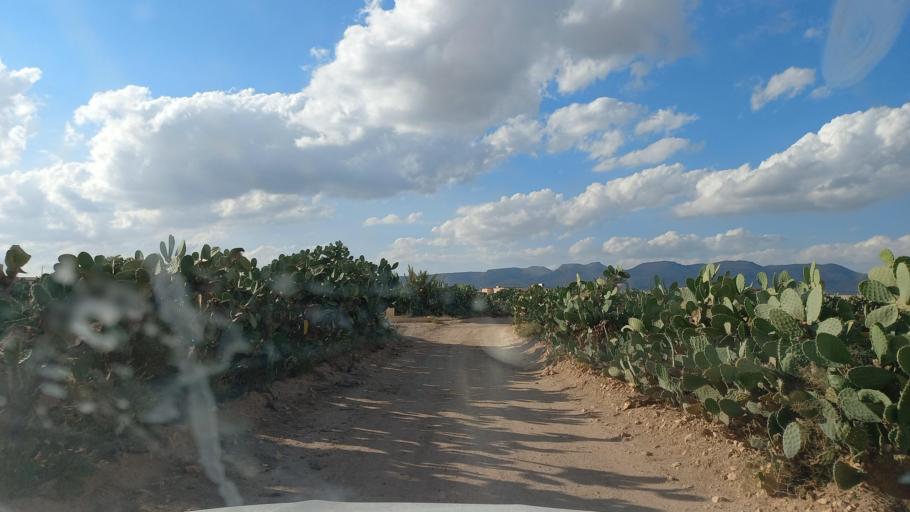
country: TN
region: Al Qasrayn
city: Sbiba
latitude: 35.3879
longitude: 9.0662
